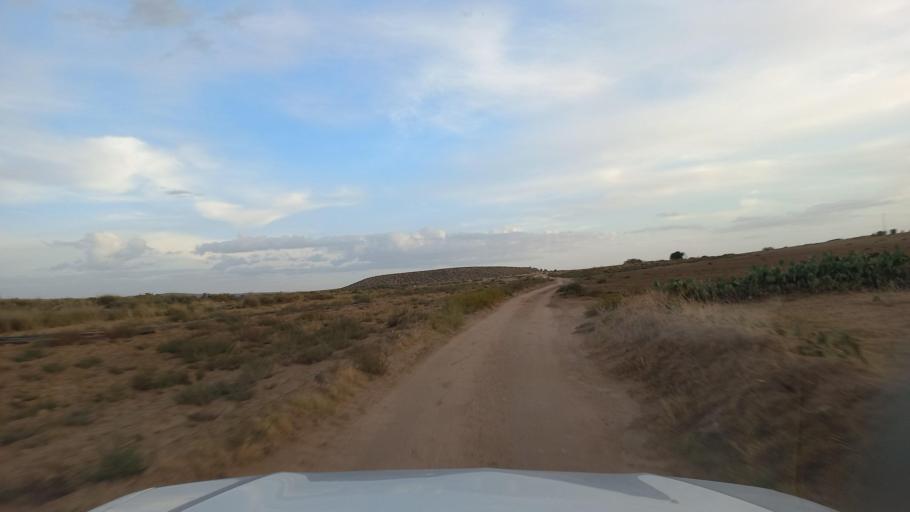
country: TN
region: Al Qasrayn
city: Sbiba
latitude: 35.4084
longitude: 9.0886
